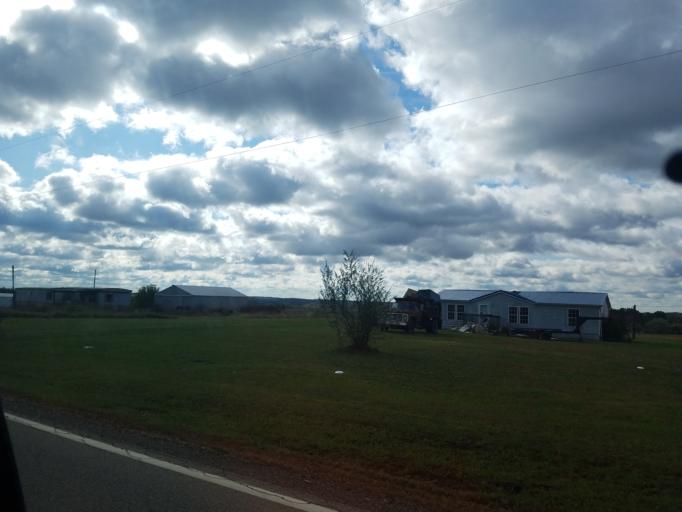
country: US
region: Ohio
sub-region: Vinton County
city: McArthur
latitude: 39.1791
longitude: -82.4587
